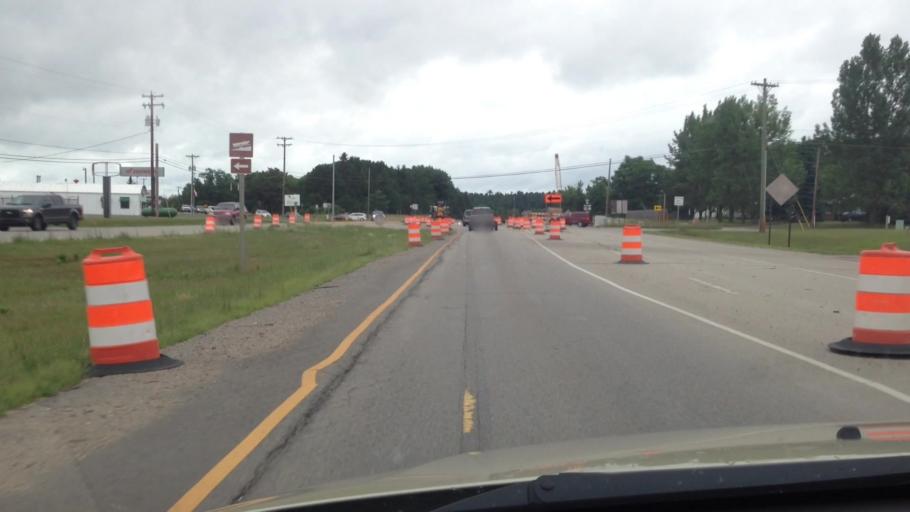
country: US
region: Michigan
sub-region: Delta County
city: Escanaba
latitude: 45.7887
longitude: -87.0812
